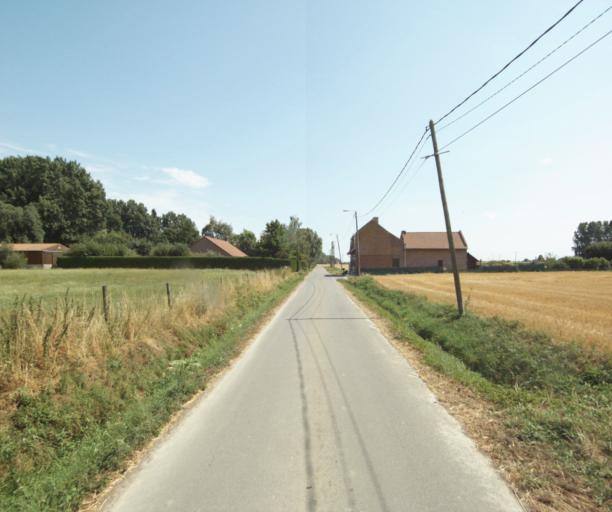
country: FR
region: Nord-Pas-de-Calais
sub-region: Departement du Nord
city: Deulemont
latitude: 50.7393
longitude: 2.9764
